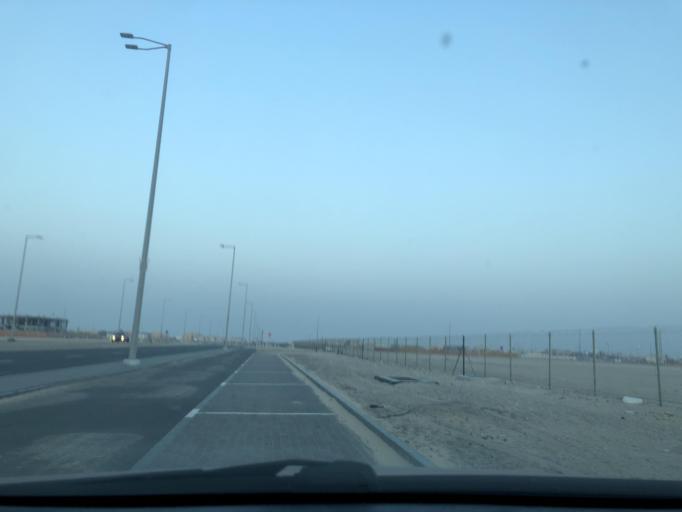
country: AE
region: Abu Dhabi
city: Abu Dhabi
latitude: 24.3603
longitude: 54.6063
